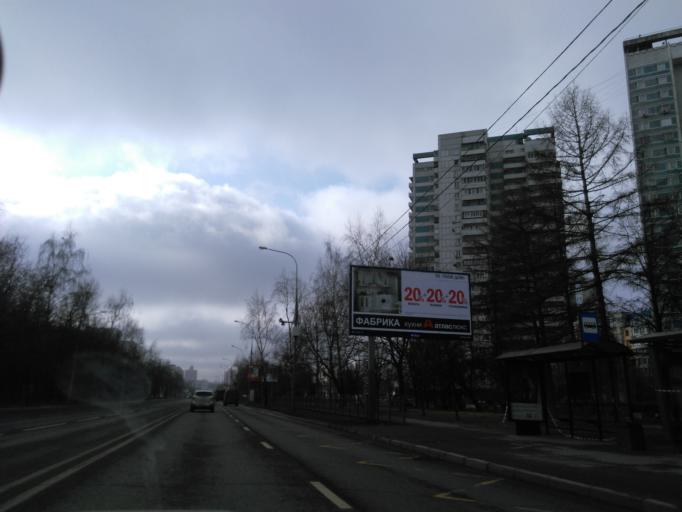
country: RU
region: Moskovskaya
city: Levoberezhnyy
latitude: 55.8545
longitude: 37.4513
